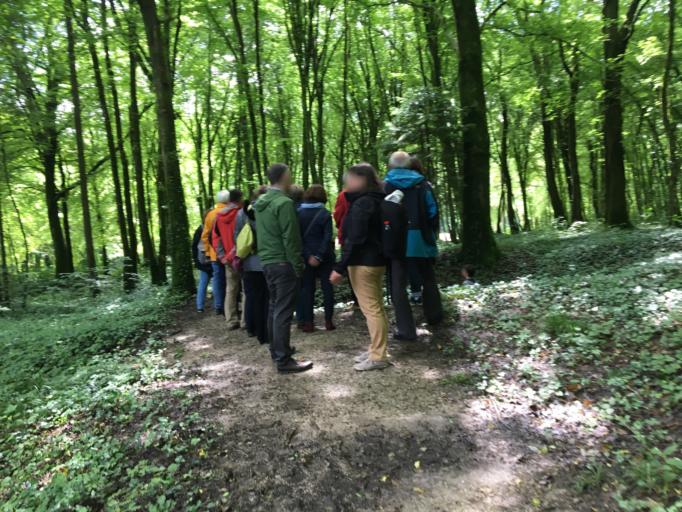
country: FR
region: Lorraine
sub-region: Departement de la Meuse
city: Belleville-sur-Meuse
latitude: 49.2723
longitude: 5.4048
